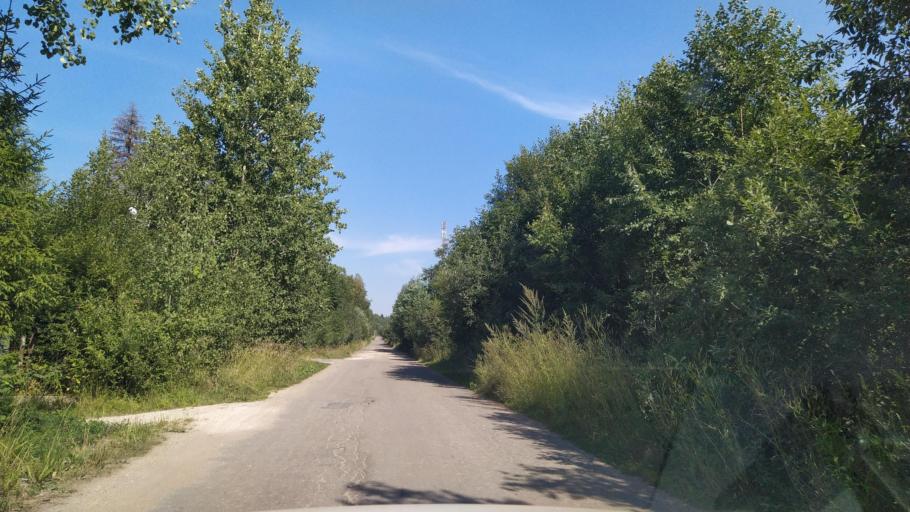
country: RU
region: Leningrad
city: Siverskiy
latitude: 59.2836
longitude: 30.0295
